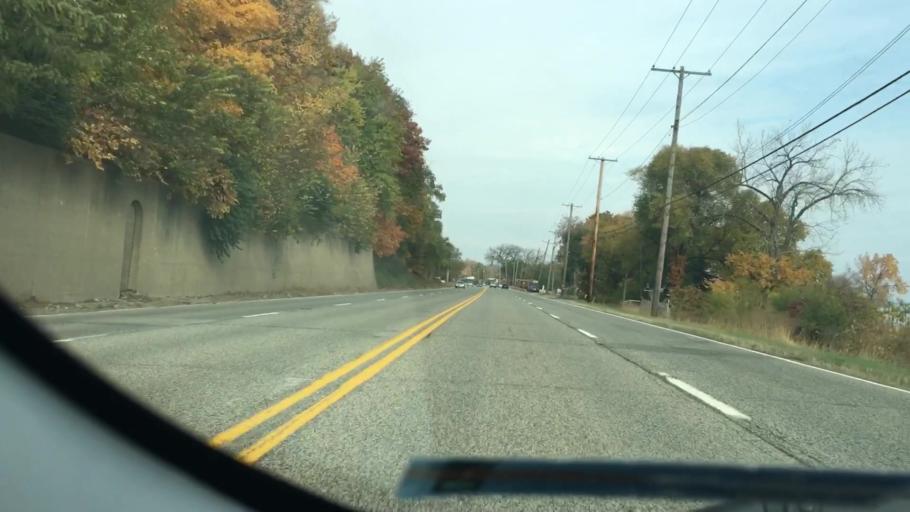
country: US
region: Illinois
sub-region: Peoria County
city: Peoria Heights
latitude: 40.7396
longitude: -89.5533
